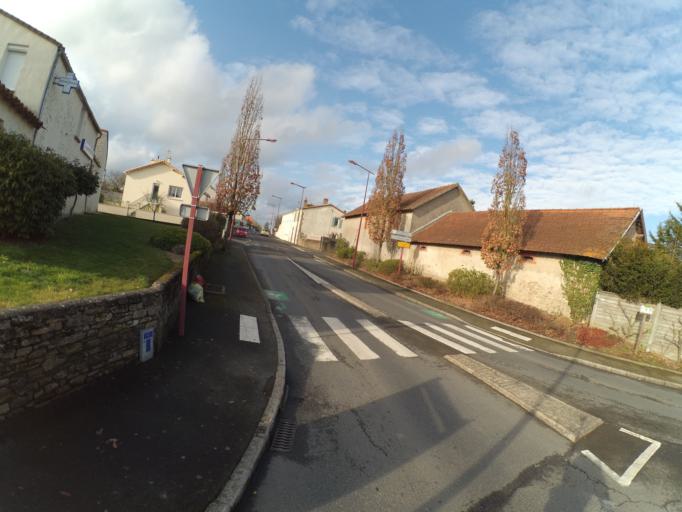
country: FR
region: Pays de la Loire
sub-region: Departement de la Loire-Atlantique
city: Clisson
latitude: 47.0793
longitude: -1.2769
